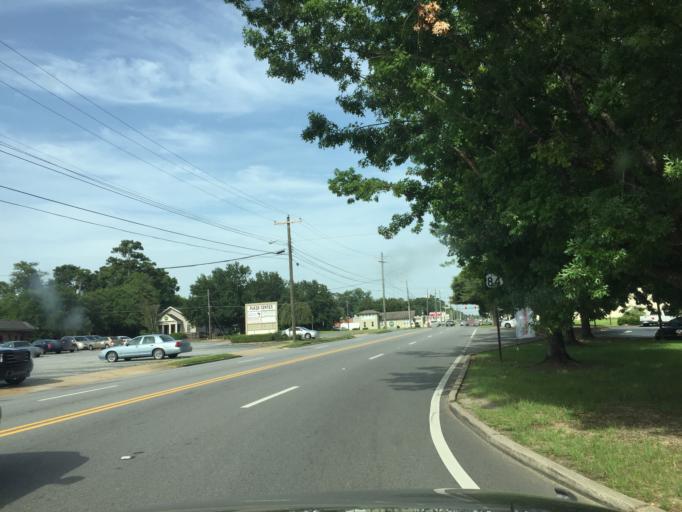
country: US
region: Georgia
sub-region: Thomas County
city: Thomasville
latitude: 30.8355
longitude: -83.9782
